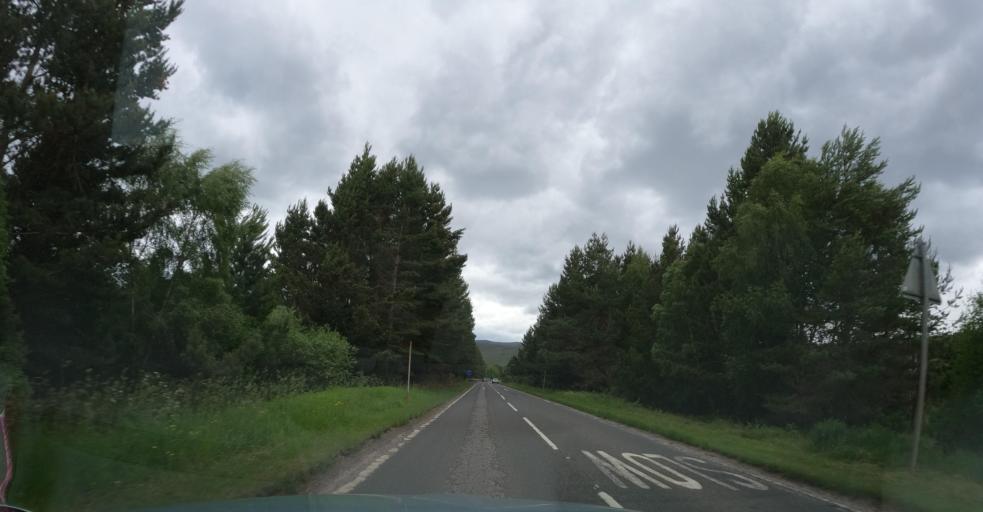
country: GB
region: Scotland
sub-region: Highland
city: Muir of Ord
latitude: 57.6356
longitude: -4.6785
